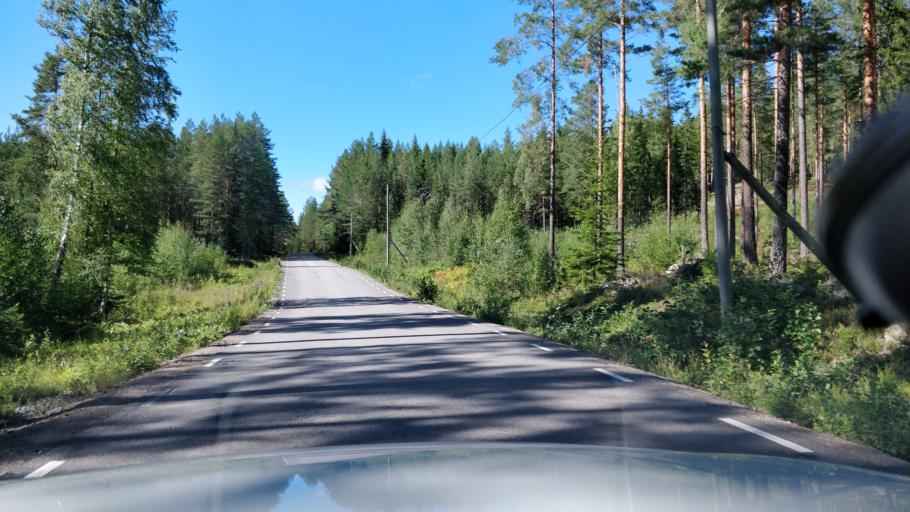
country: SE
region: Dalarna
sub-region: Faluns Kommun
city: Bjursas
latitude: 60.7430
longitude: 15.5358
